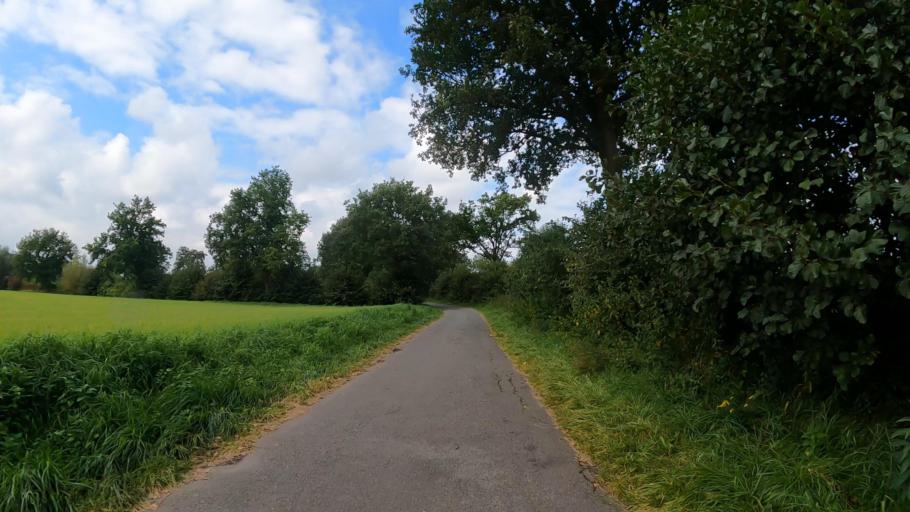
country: DE
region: Schleswig-Holstein
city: Kolln-Reisiek
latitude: 53.7299
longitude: 9.6834
